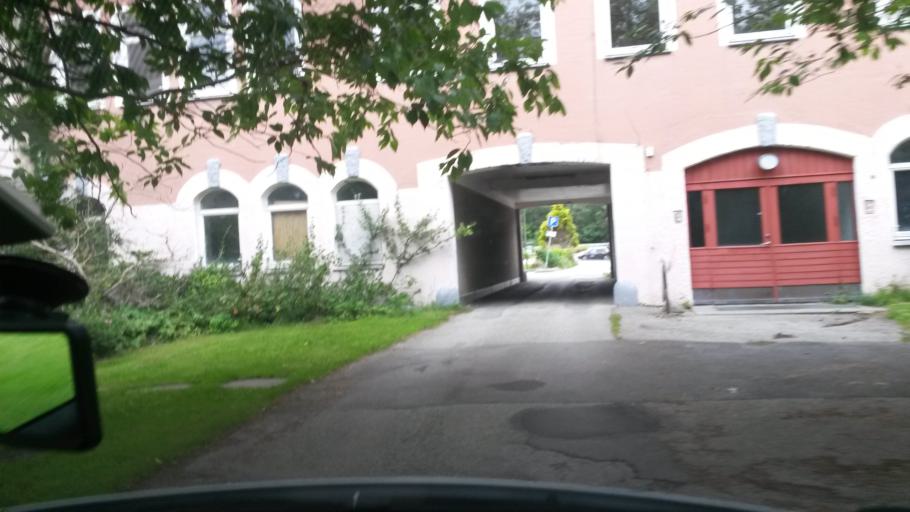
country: NO
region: Rogaland
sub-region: Sandnes
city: Sandnes
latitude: 58.9003
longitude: 5.7801
